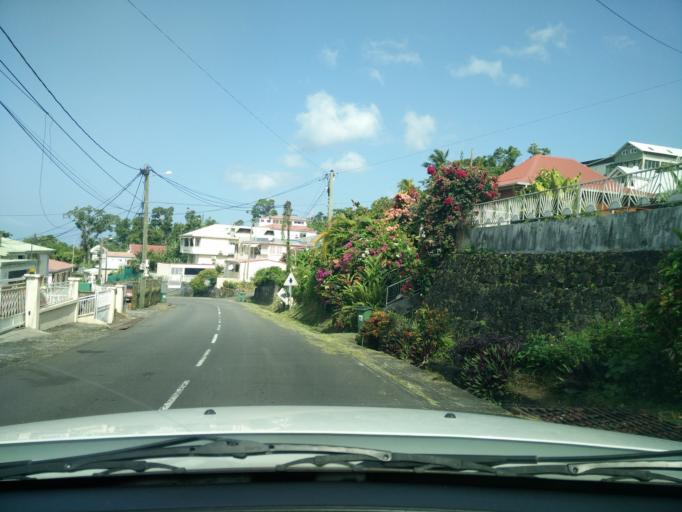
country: GP
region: Guadeloupe
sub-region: Guadeloupe
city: Gourbeyre
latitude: 16.0003
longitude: -61.6969
